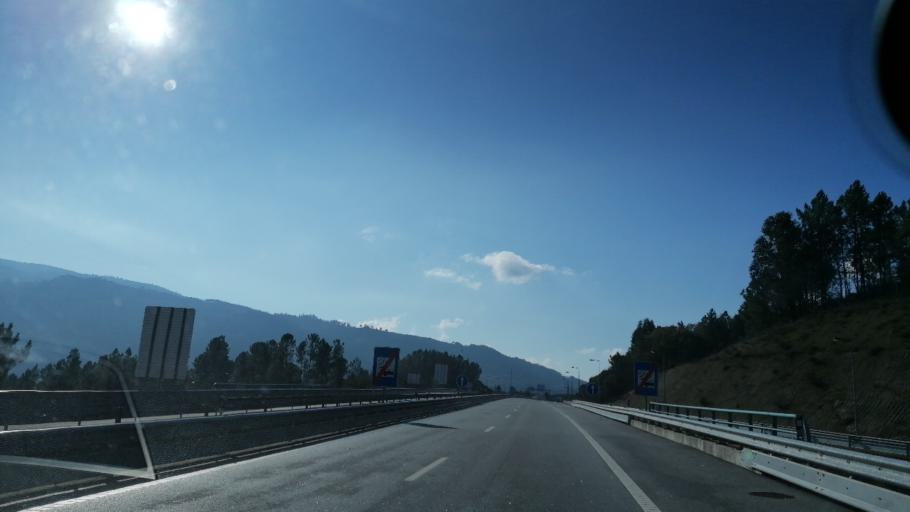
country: PT
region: Porto
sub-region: Amarante
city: Amarante
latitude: 41.2596
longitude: -8.0323
